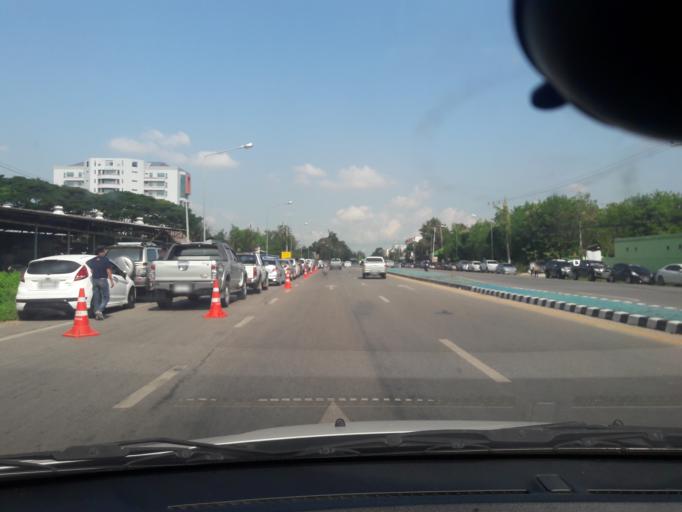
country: TH
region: Lampang
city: Lampang
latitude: 18.2291
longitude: 99.4904
